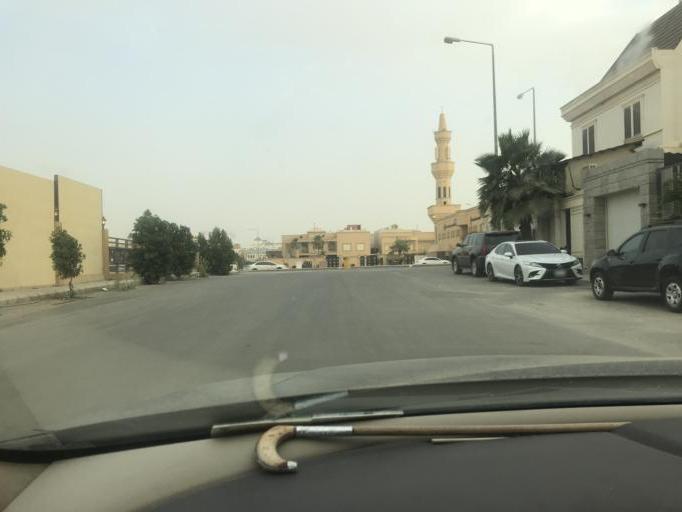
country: SA
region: Ar Riyad
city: Riyadh
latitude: 24.8075
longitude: 46.6685
